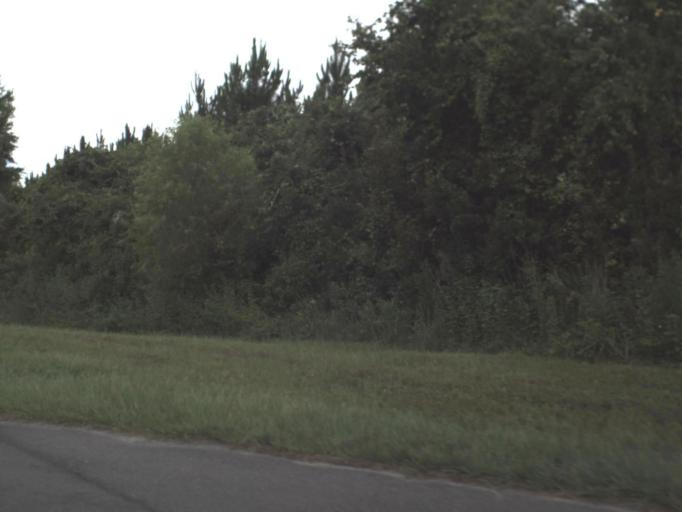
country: US
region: Florida
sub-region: Columbia County
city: Five Points
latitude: 30.3336
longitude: -82.6257
